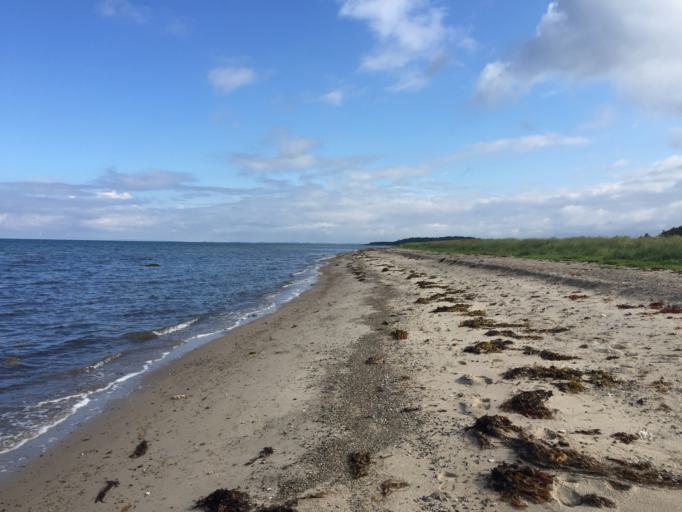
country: DK
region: Zealand
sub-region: Slagelse Kommune
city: Korsor
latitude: 55.2308
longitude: 11.1706
